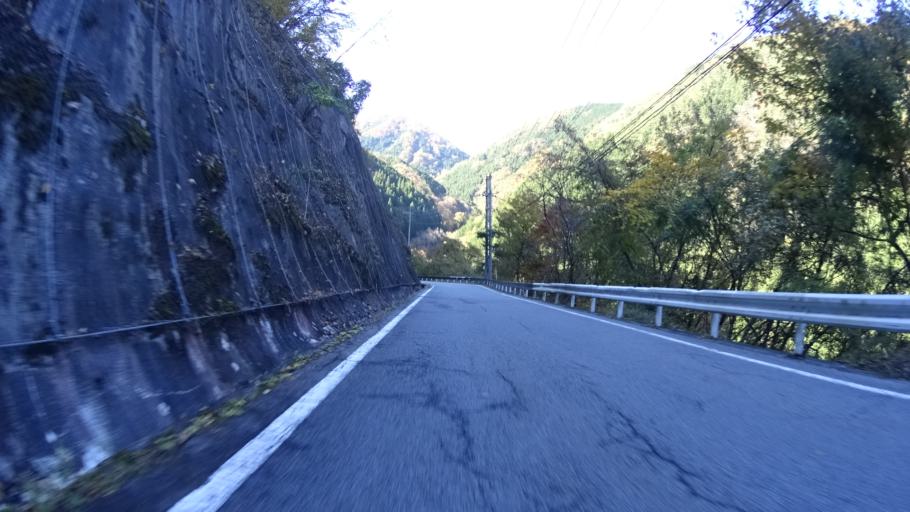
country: JP
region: Yamanashi
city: Otsuki
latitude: 35.7805
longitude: 138.9203
